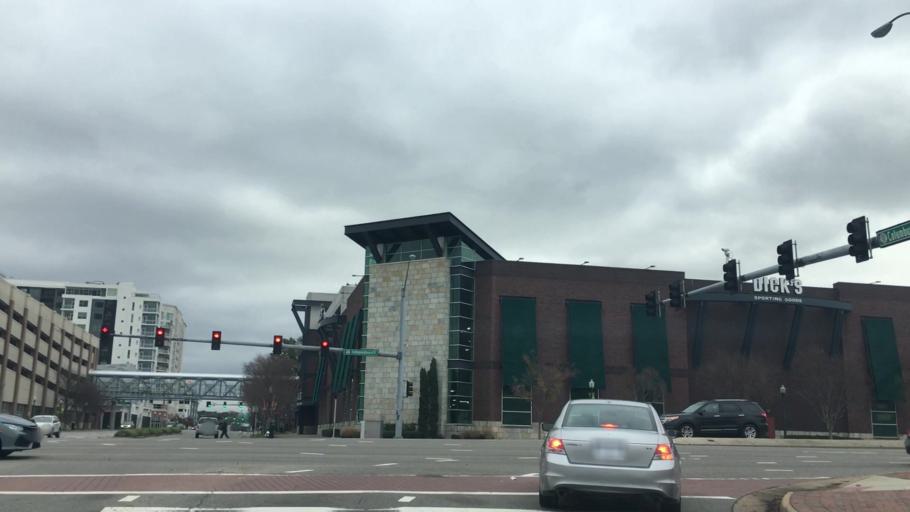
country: US
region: Virginia
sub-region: City of Chesapeake
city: Chesapeake
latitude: 36.8409
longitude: -76.1372
